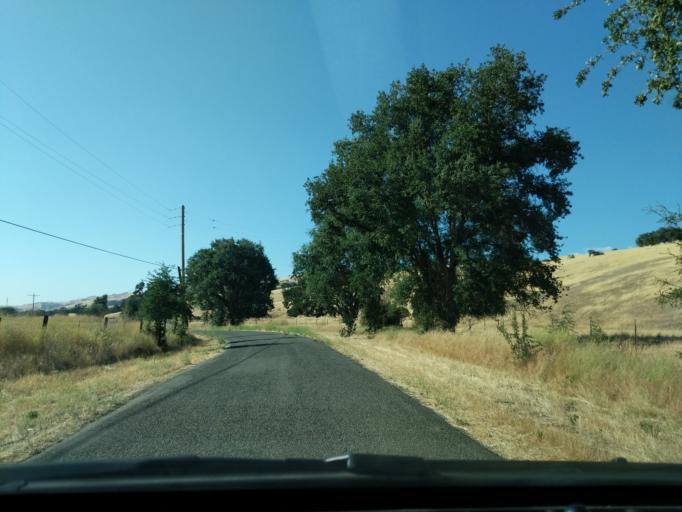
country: US
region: California
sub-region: Monterey County
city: King City
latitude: 36.1434
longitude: -120.7535
